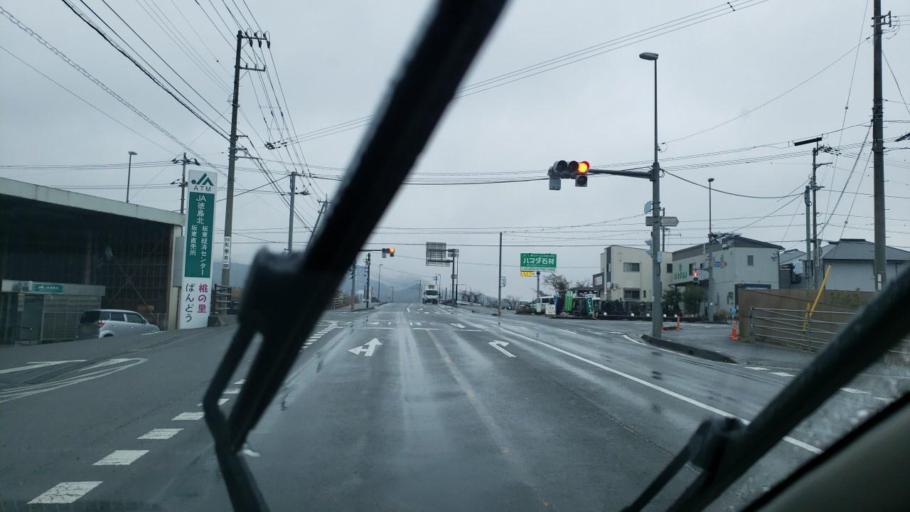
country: JP
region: Tokushima
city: Ishii
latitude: 34.1576
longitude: 134.4976
